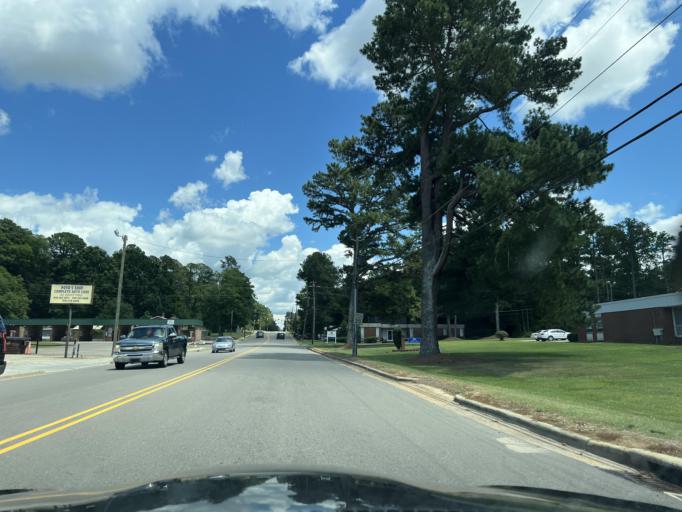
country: US
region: North Carolina
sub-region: Lee County
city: Sanford
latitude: 35.4692
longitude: -79.1710
